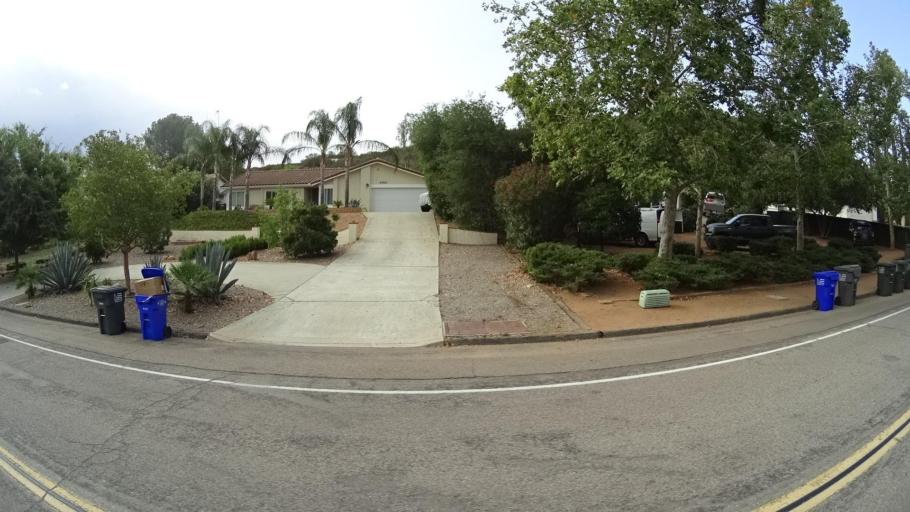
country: US
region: California
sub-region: San Diego County
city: San Diego Country Estates
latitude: 33.0095
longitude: -116.8011
